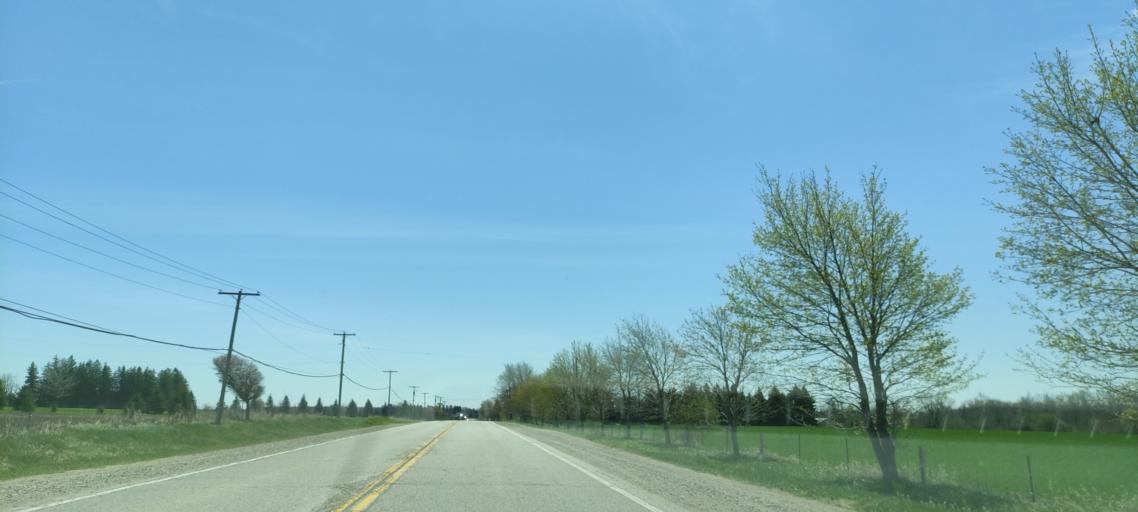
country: CA
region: Ontario
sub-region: Wellington County
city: Guelph
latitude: 43.6021
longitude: -80.3257
